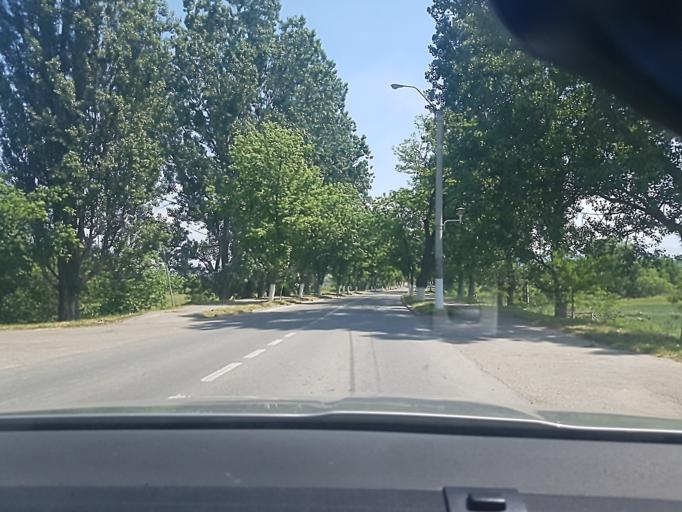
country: RO
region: Hunedoara
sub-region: Comuna Calan
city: Calan
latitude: 45.7351
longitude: 23.0092
